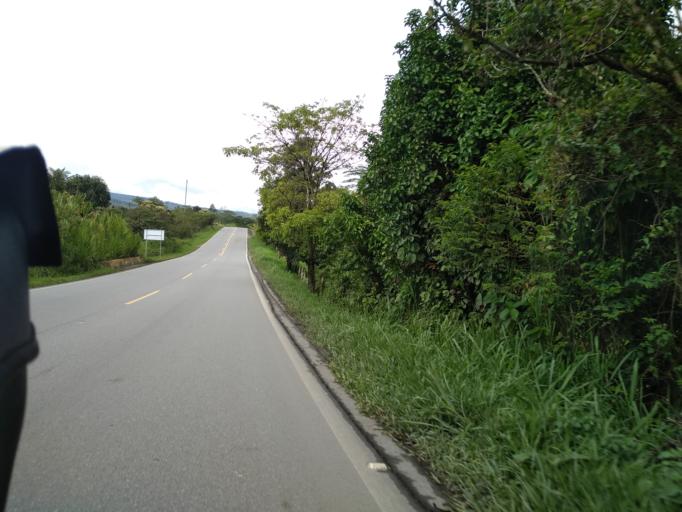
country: CO
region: Santander
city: Suaita
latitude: 6.1290
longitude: -73.3613
